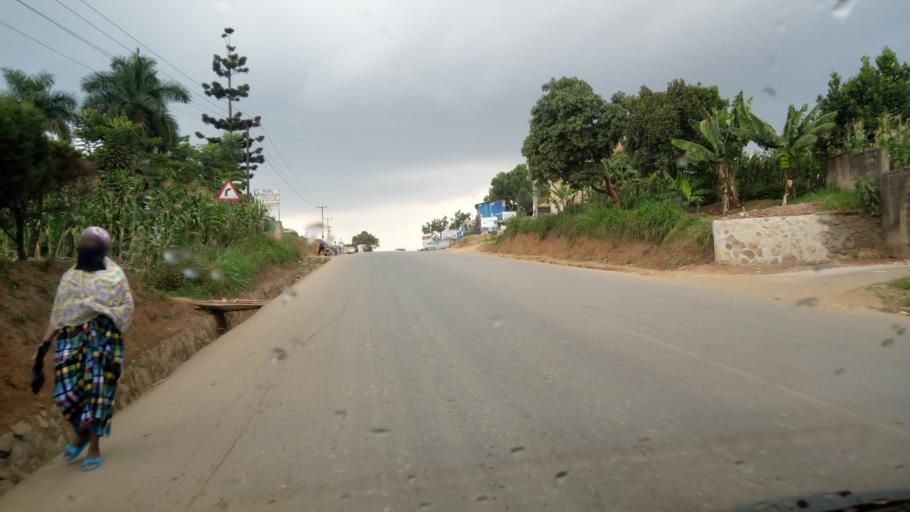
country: UG
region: Central Region
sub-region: Wakiso District
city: Wakiso
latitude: 0.4046
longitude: 32.5433
